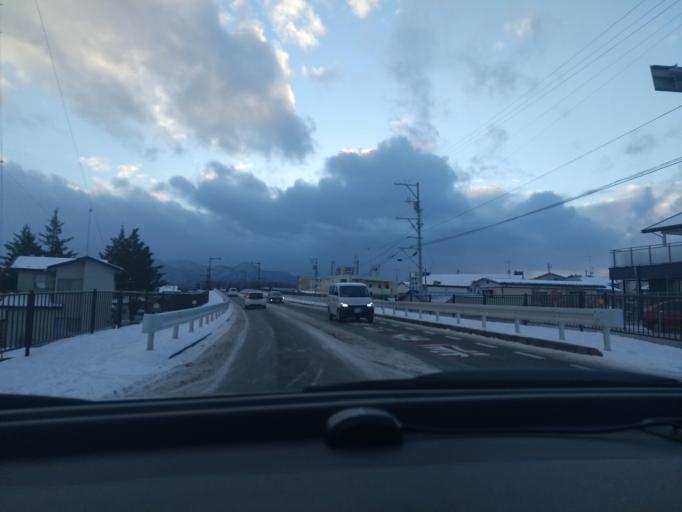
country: JP
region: Iwate
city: Morioka-shi
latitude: 39.7112
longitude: 141.1184
